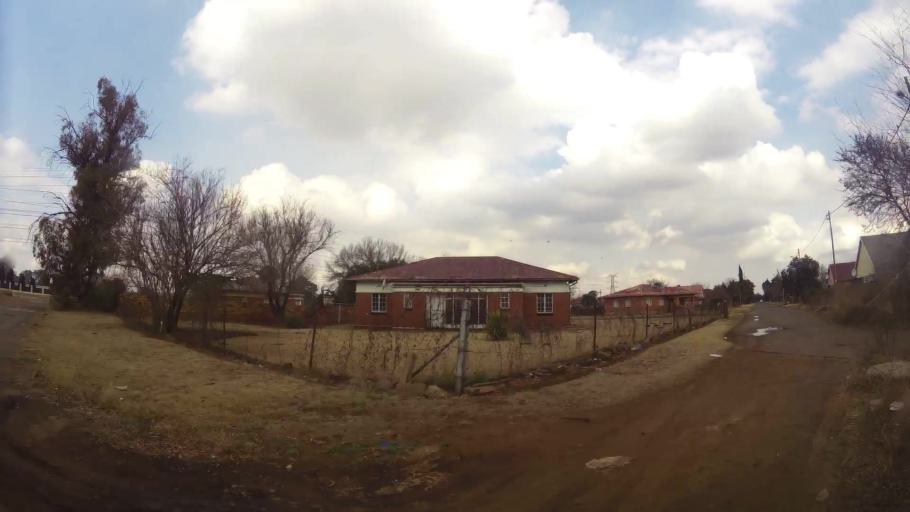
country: ZA
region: Gauteng
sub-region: Sedibeng District Municipality
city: Vereeniging
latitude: -26.6724
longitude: 27.9375
